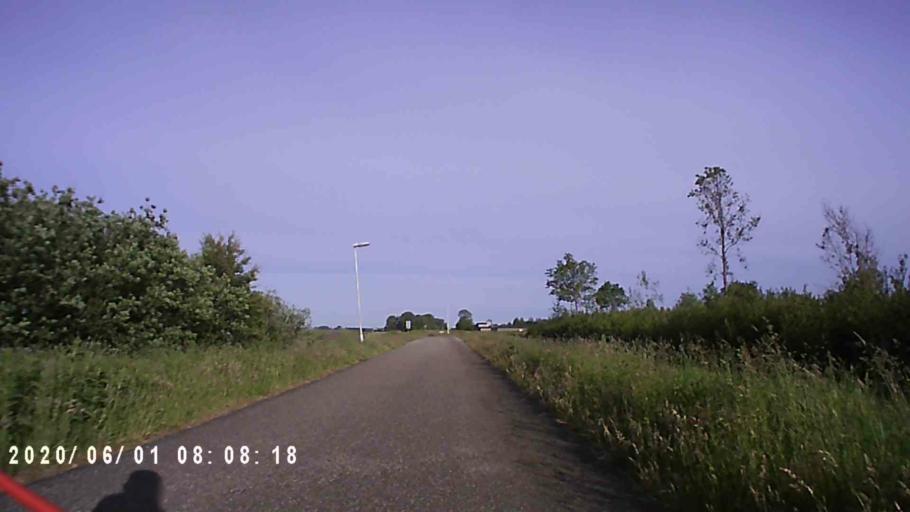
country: NL
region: Friesland
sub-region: Gemeente Ferwerderadiel
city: Burdaard
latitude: 53.2838
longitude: 5.8987
